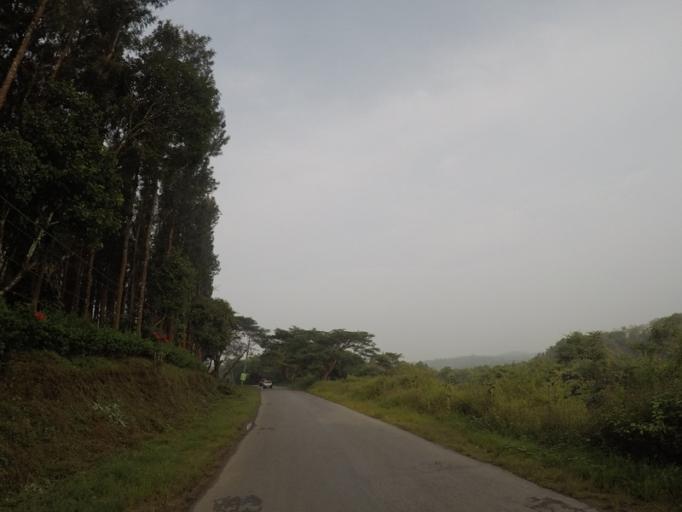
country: IN
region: Karnataka
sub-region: Chikmagalur
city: Mudigere
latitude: 13.2561
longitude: 75.6651
